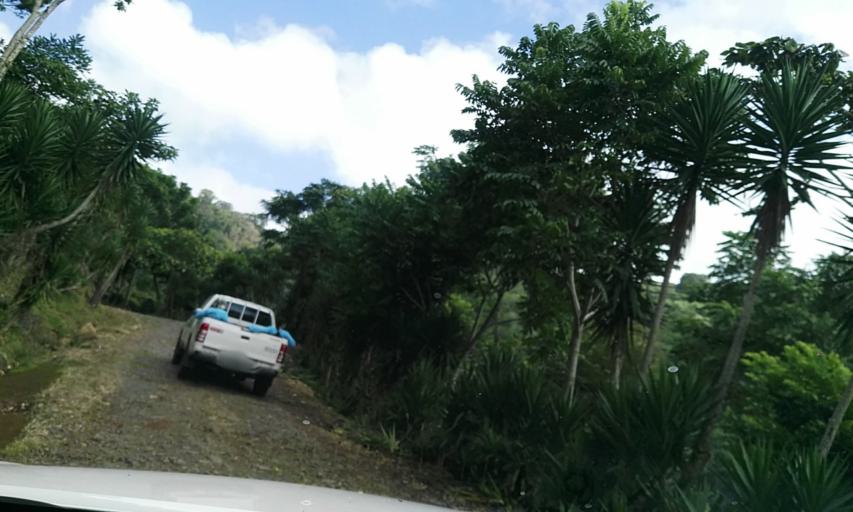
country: NI
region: Matagalpa
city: Matagalpa
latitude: 13.0155
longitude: -85.8789
